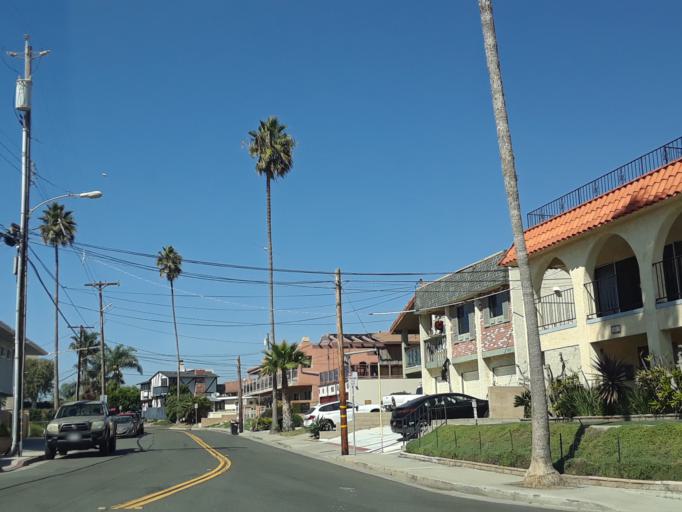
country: US
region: California
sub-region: Orange County
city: San Clemente
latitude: 33.4284
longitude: -117.6280
